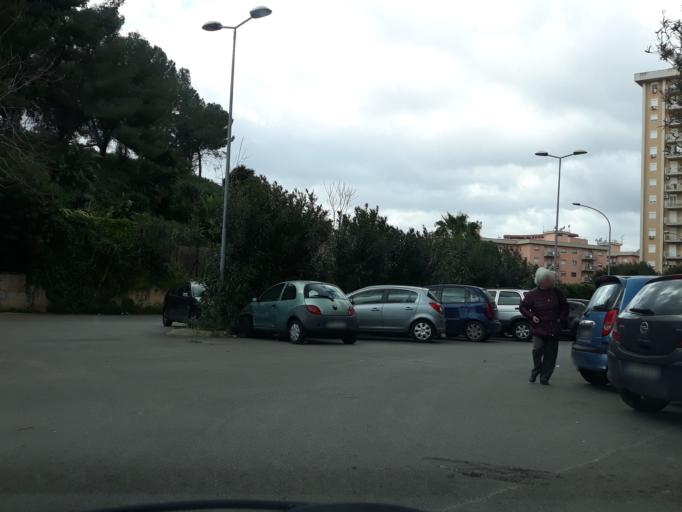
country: IT
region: Sicily
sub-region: Palermo
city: Palermo
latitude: 38.1135
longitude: 13.3382
